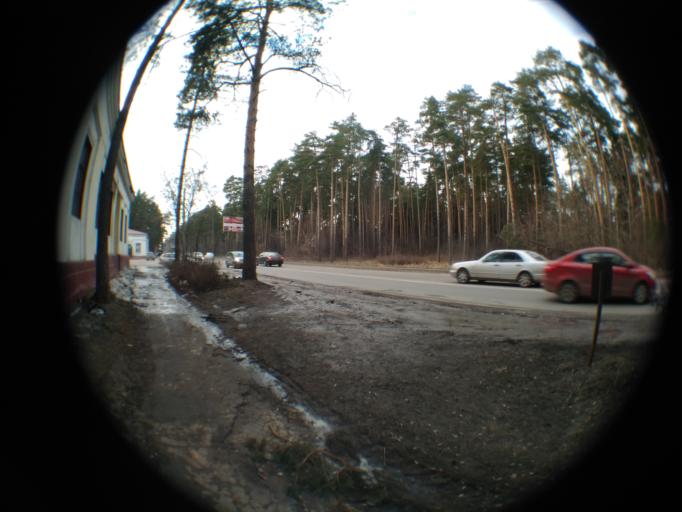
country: RU
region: Moskovskaya
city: Kratovo
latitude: 55.5777
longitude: 38.1588
